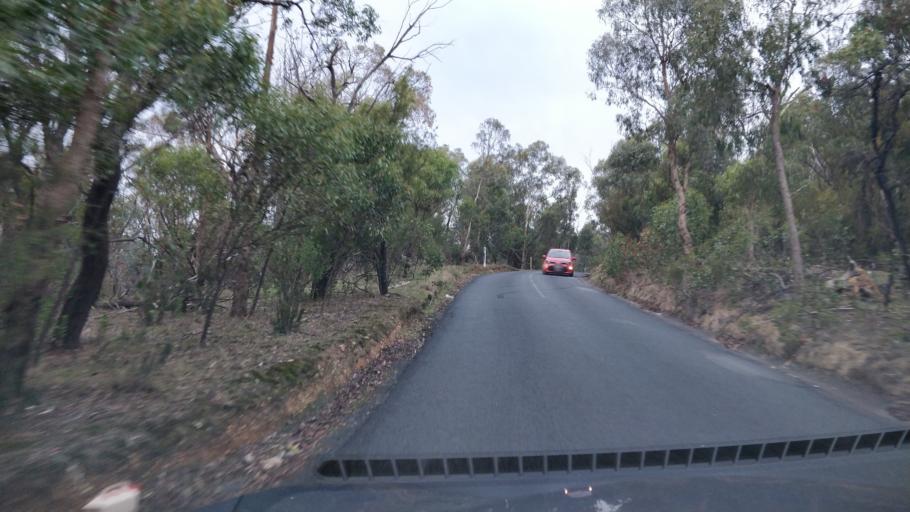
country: AU
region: Victoria
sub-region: Nillumbik
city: Research
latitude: -37.6876
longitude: 145.1774
